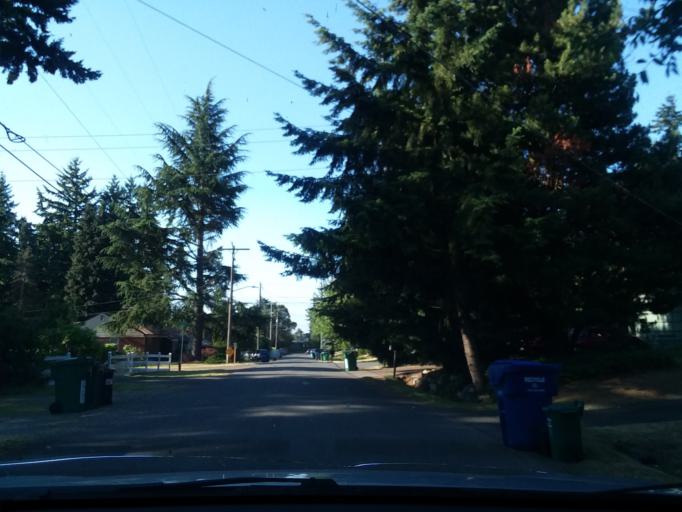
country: US
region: Washington
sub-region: King County
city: Shoreline
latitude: 47.7181
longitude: -122.3262
